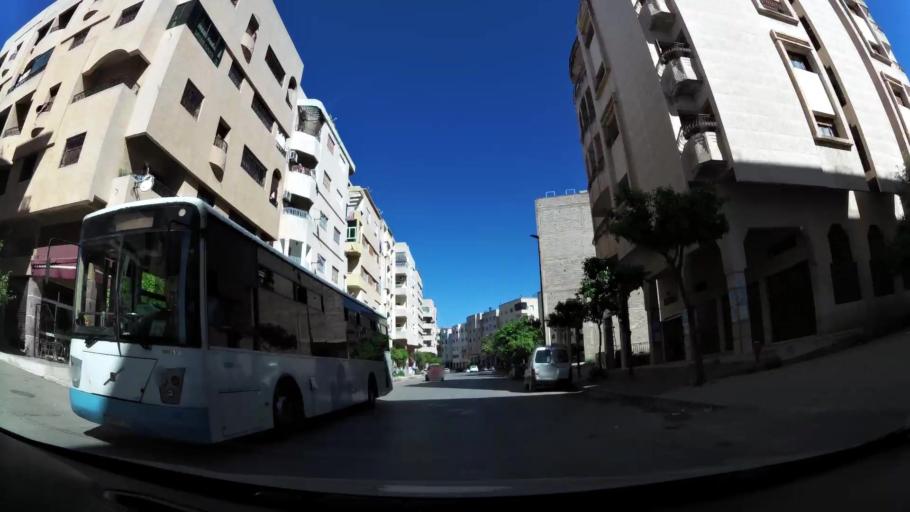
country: MA
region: Fes-Boulemane
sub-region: Fes
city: Fes
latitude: 34.0151
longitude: -4.9739
